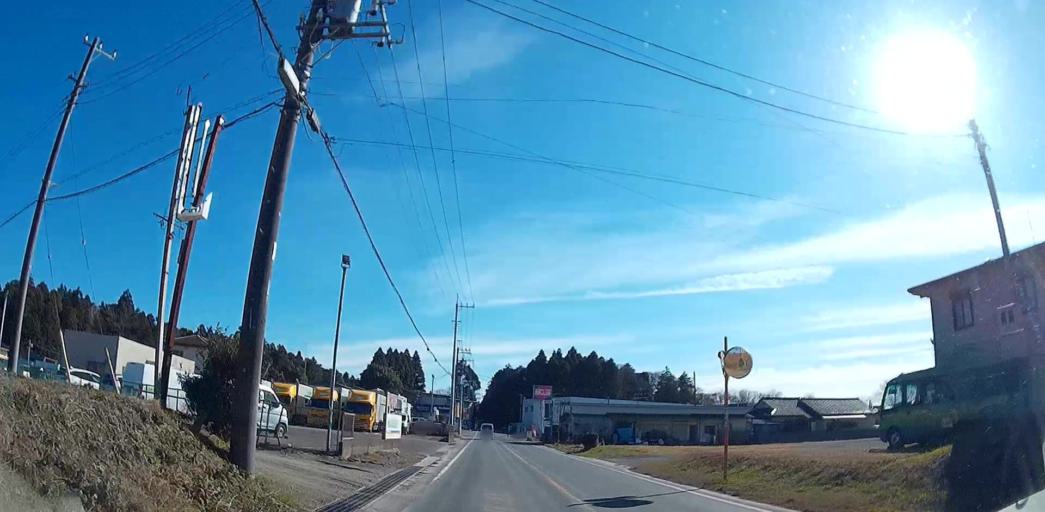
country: JP
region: Chiba
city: Narita
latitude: 35.7859
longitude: 140.4043
